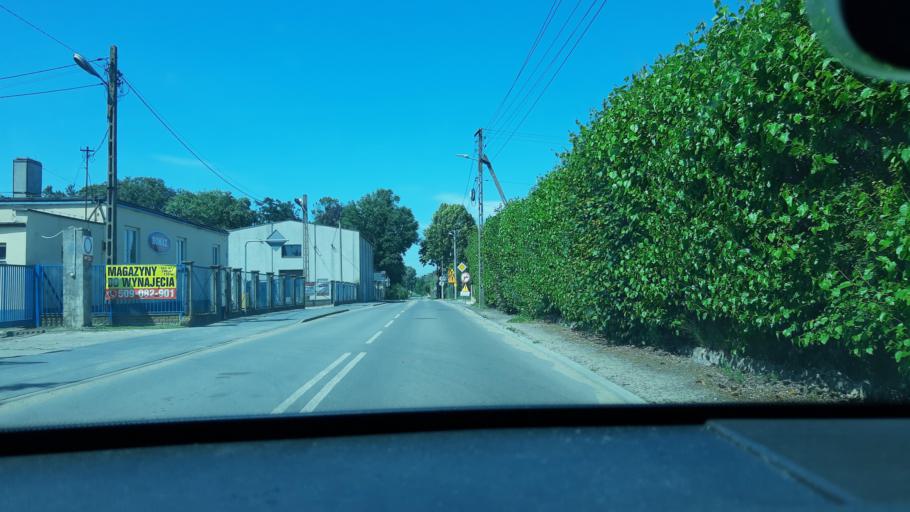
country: PL
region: Lodz Voivodeship
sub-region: Powiat zdunskowolski
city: Zdunska Wola
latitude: 51.6117
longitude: 18.9382
